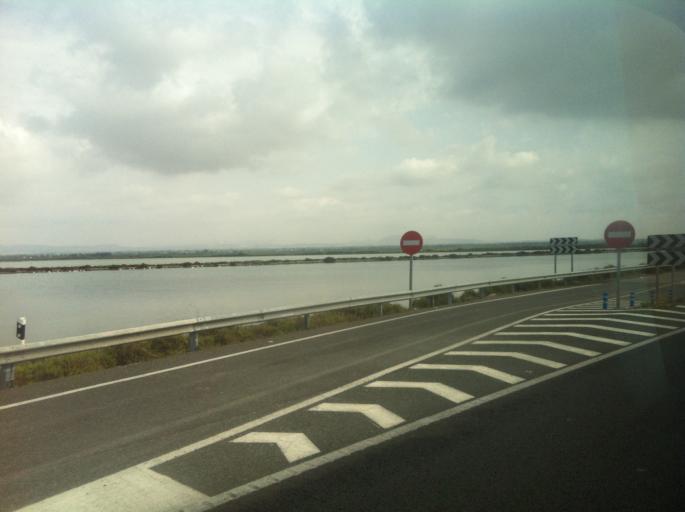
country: ES
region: Valencia
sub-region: Provincia de Alicante
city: Santa Pola
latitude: 38.1836
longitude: -0.6158
